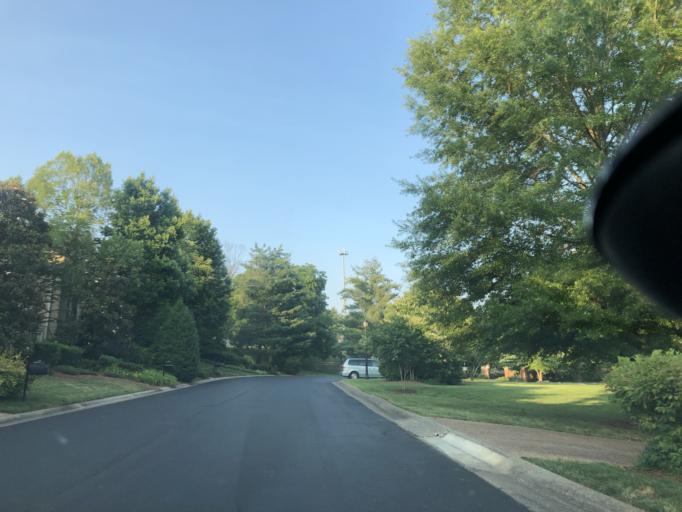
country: US
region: Tennessee
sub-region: Davidson County
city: Belle Meade
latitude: 36.1267
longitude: -86.8190
